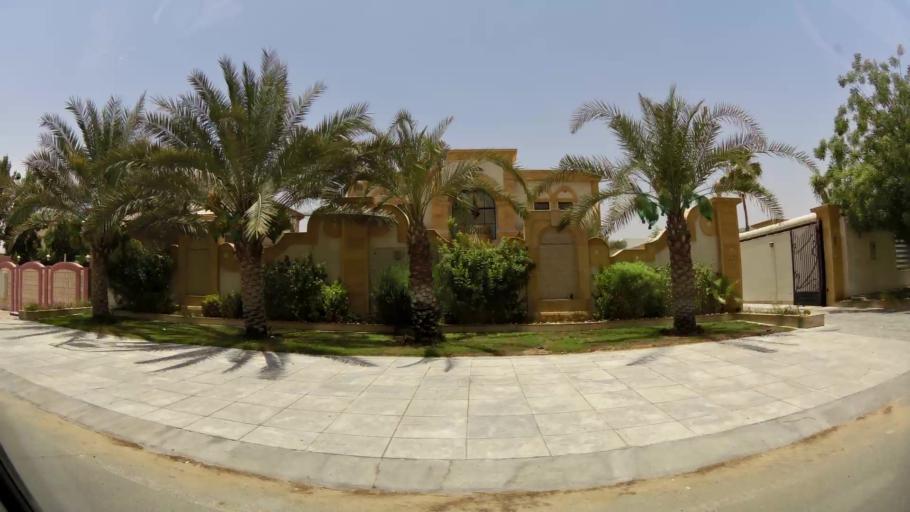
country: AE
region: Ash Shariqah
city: Sharjah
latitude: 25.2370
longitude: 55.4539
